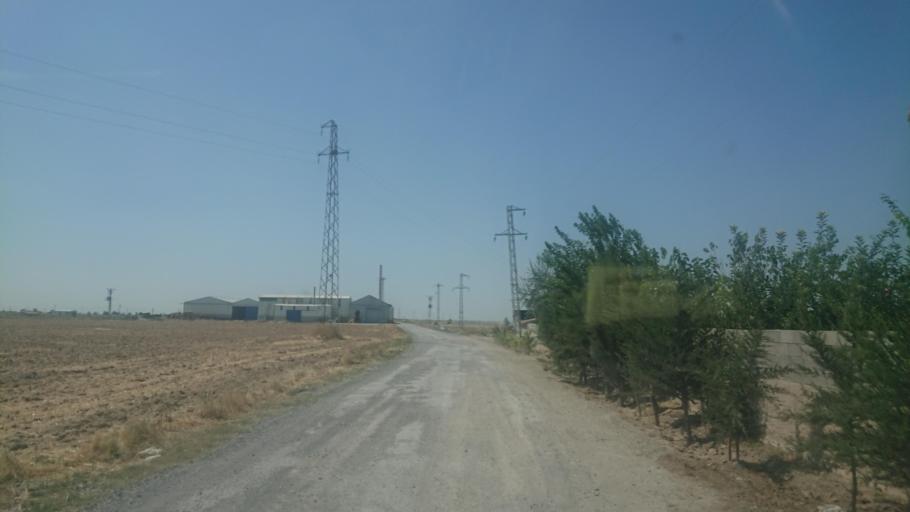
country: TR
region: Aksaray
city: Sultanhani
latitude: 38.2849
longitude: 33.7110
